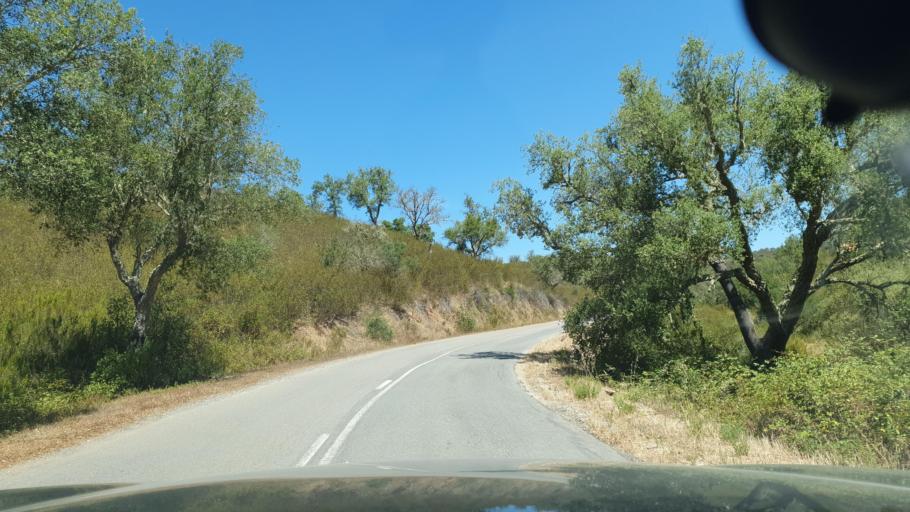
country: PT
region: Beja
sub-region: Odemira
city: Odemira
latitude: 37.5301
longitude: -8.4716
